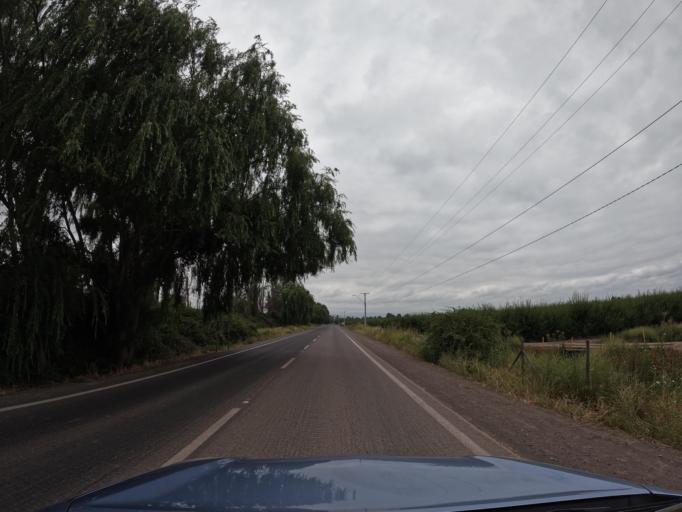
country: CL
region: O'Higgins
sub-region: Provincia de Colchagua
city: Chimbarongo
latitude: -34.7279
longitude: -71.0790
